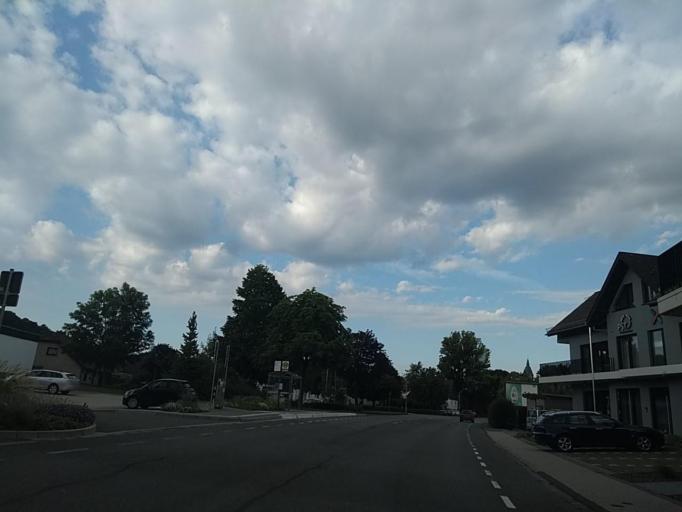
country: DE
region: North Rhine-Westphalia
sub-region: Regierungsbezirk Arnsberg
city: Brilon
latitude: 51.3967
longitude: 8.5806
